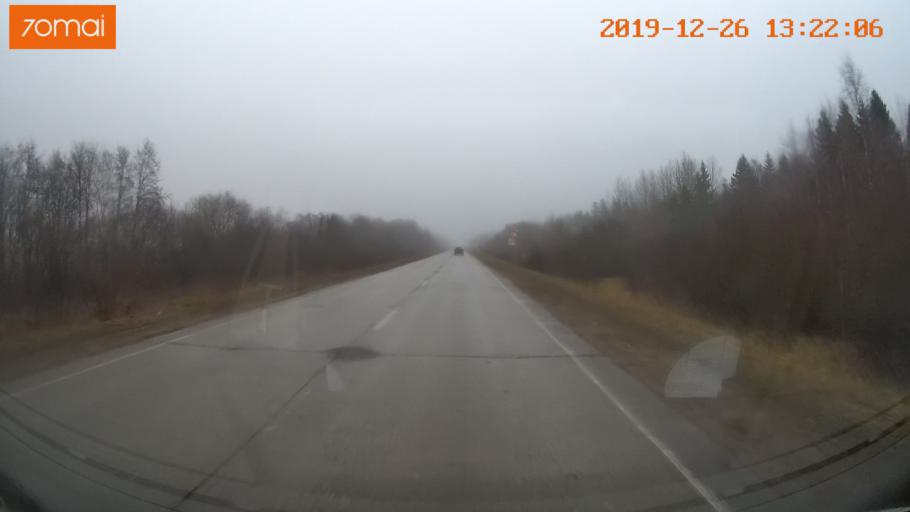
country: RU
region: Vologda
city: Cherepovets
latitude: 58.9056
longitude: 38.1675
